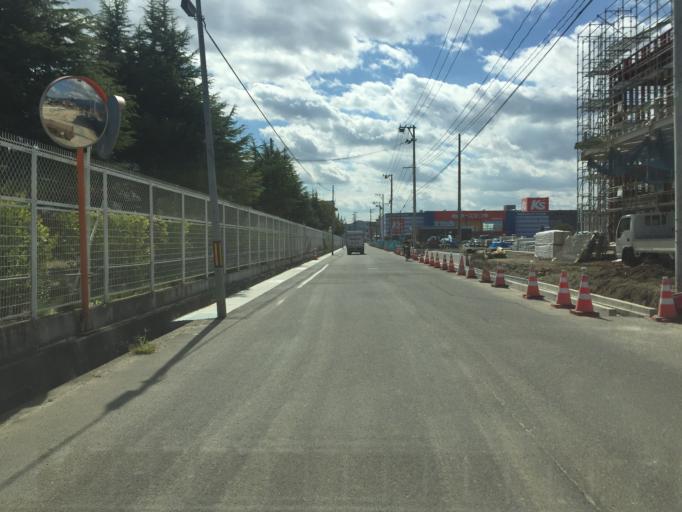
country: JP
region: Fukushima
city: Fukushima-shi
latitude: 37.7305
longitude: 140.4545
